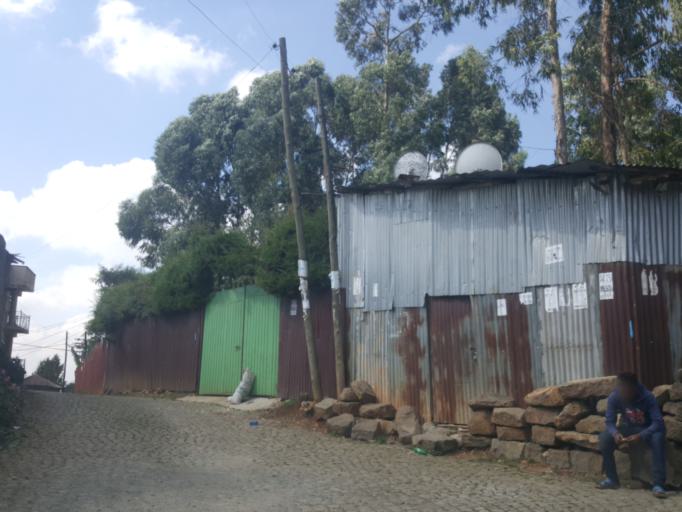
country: ET
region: Adis Abeba
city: Addis Ababa
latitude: 9.0530
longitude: 38.7257
